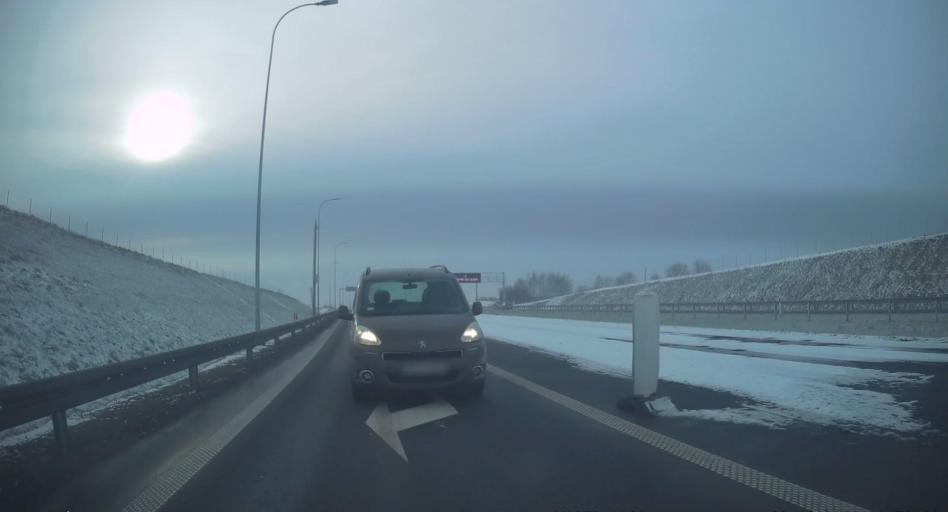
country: PL
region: Lesser Poland Voivodeship
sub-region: Powiat miechowski
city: Miechow
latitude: 50.3118
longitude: 20.0350
